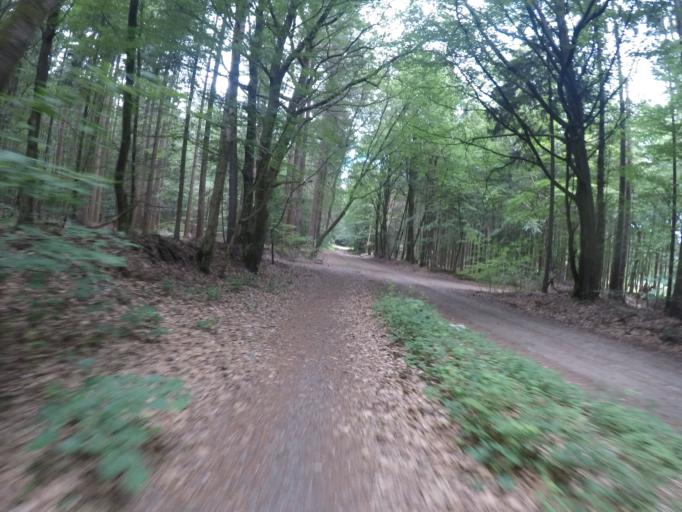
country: DE
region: Lower Saxony
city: Wingst
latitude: 53.7248
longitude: 9.0678
